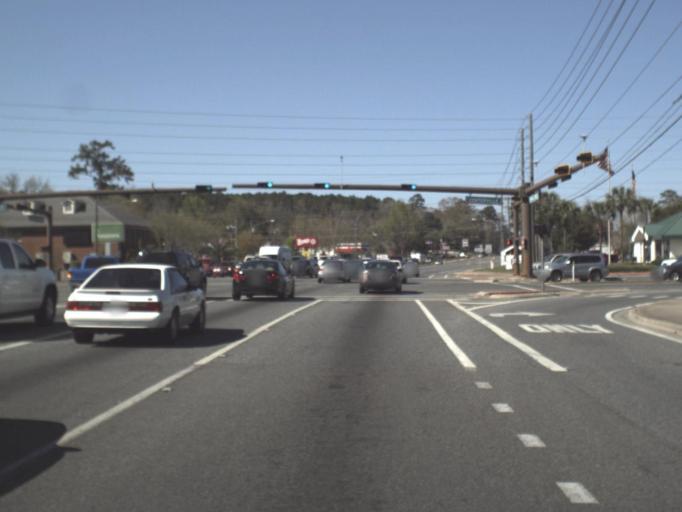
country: US
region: Florida
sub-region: Leon County
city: Tallahassee
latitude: 30.4777
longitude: -84.2364
